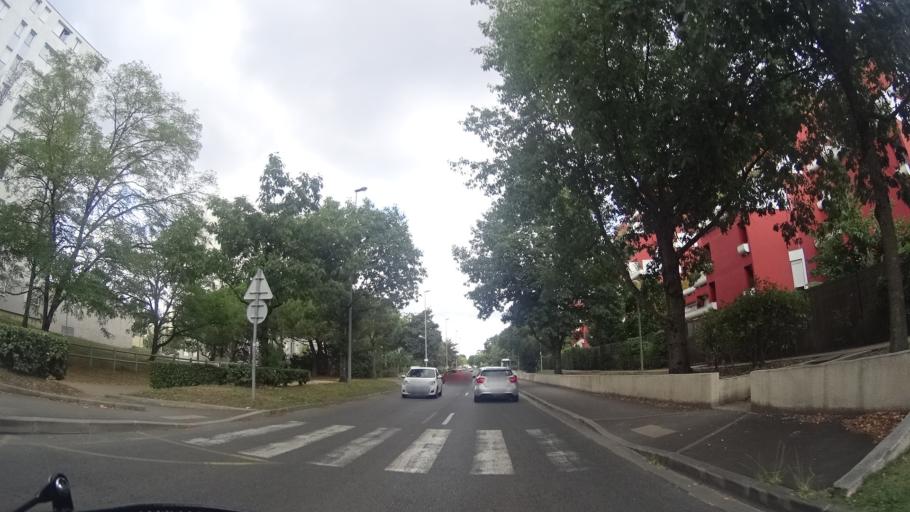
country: FR
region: Aquitaine
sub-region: Departement de la Gironde
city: Talence
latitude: 44.7930
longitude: -0.5847
